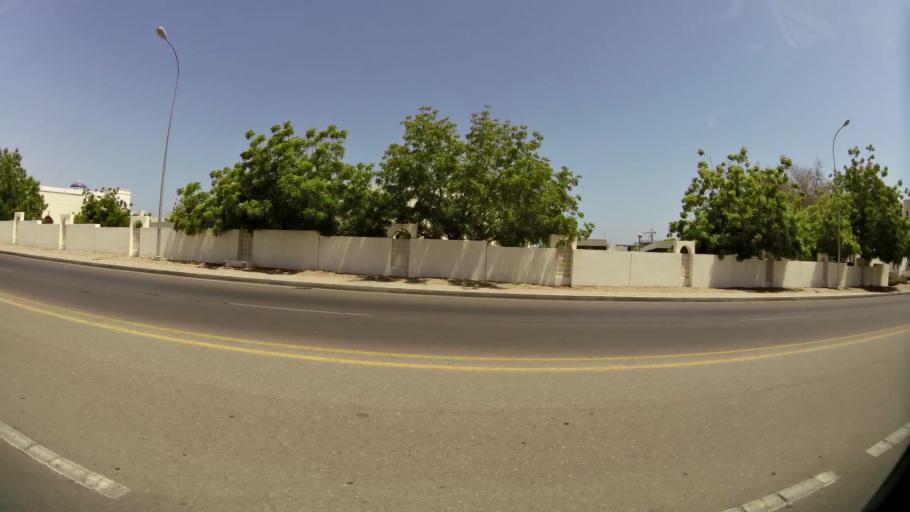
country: OM
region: Muhafazat Masqat
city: Bawshar
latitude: 23.5977
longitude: 58.4223
